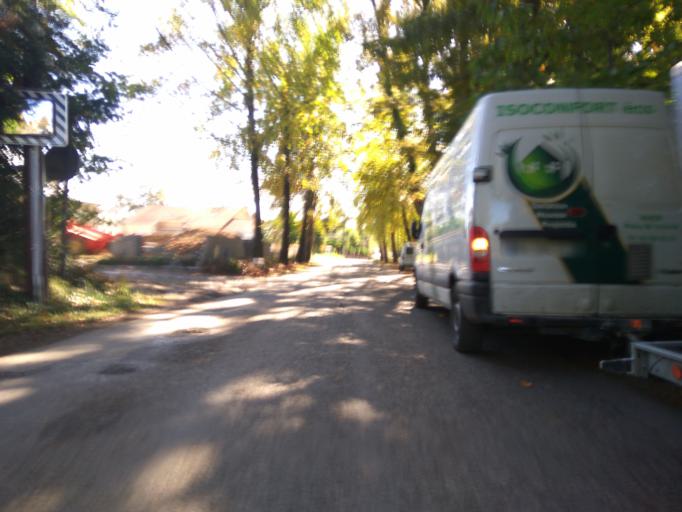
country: FR
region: Aquitaine
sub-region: Departement des Pyrenees-Atlantiques
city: Idron
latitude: 43.2990
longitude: -0.3134
